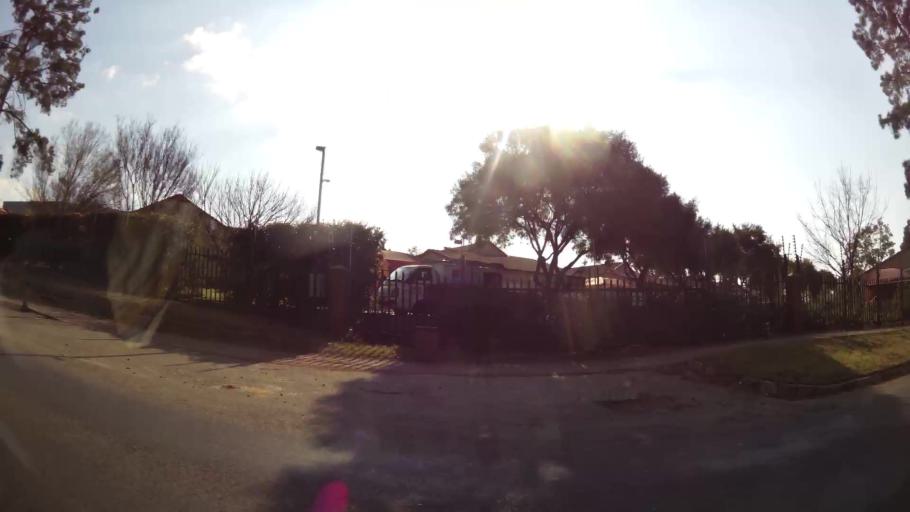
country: ZA
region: Gauteng
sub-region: City of Johannesburg Metropolitan Municipality
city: Modderfontein
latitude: -26.1061
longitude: 28.1495
